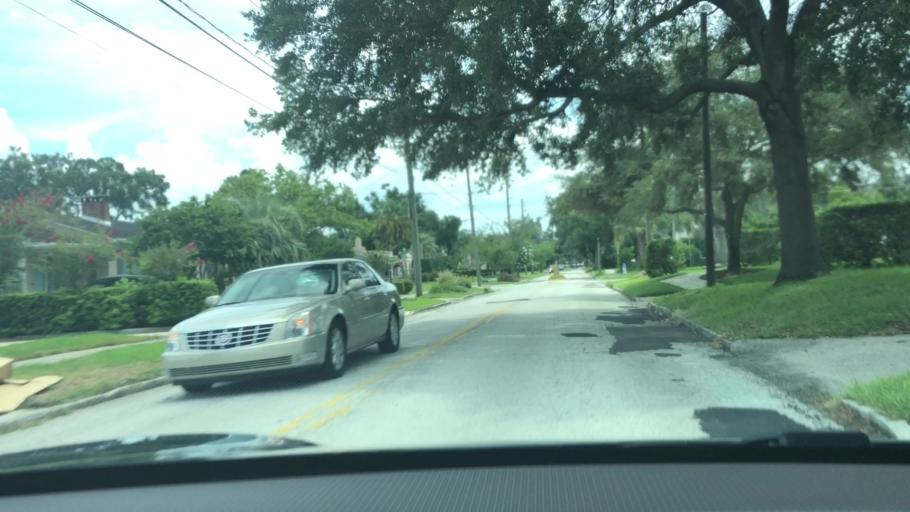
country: US
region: Florida
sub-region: Orange County
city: Orlando
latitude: 28.5191
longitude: -81.3723
